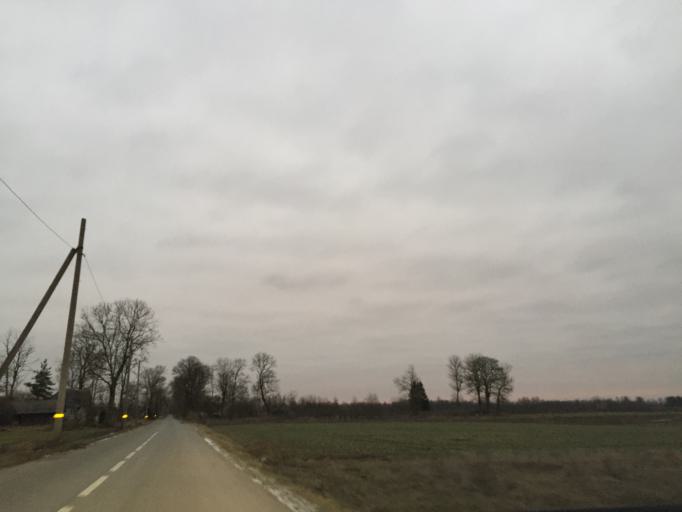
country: LT
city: Zagare
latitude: 56.3337
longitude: 23.2867
